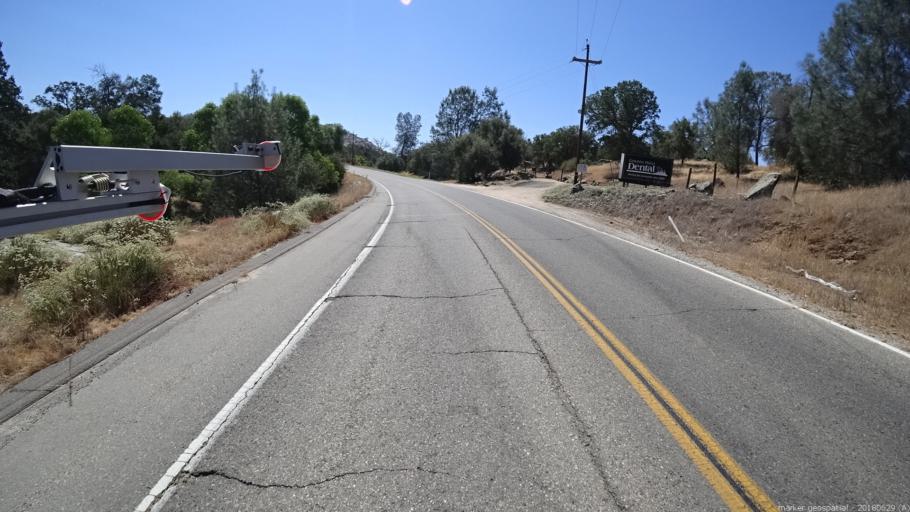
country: US
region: California
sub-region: Madera County
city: Yosemite Lakes
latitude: 37.1553
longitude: -119.7369
